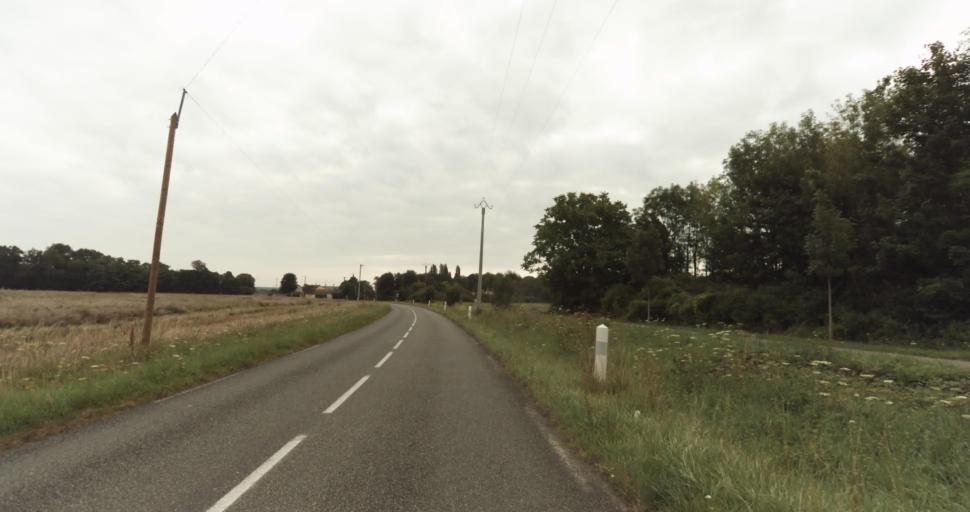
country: FR
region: Centre
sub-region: Departement d'Eure-et-Loir
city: Sorel-Moussel
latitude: 48.8348
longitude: 1.3584
